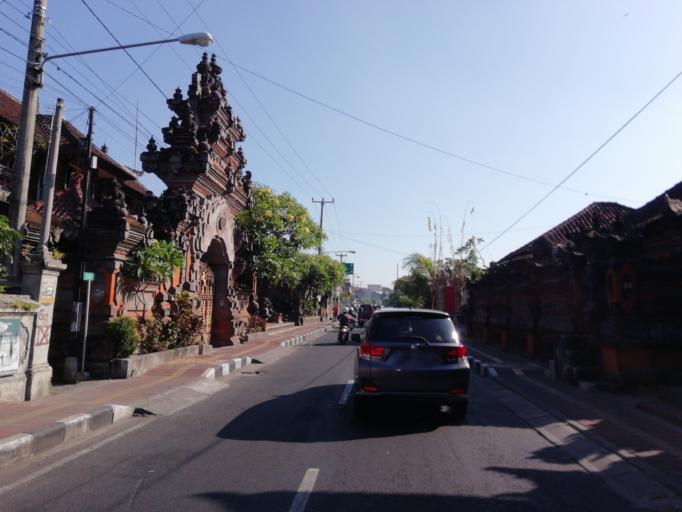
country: ID
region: Bali
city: Denpasar
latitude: -8.6516
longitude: 115.2088
